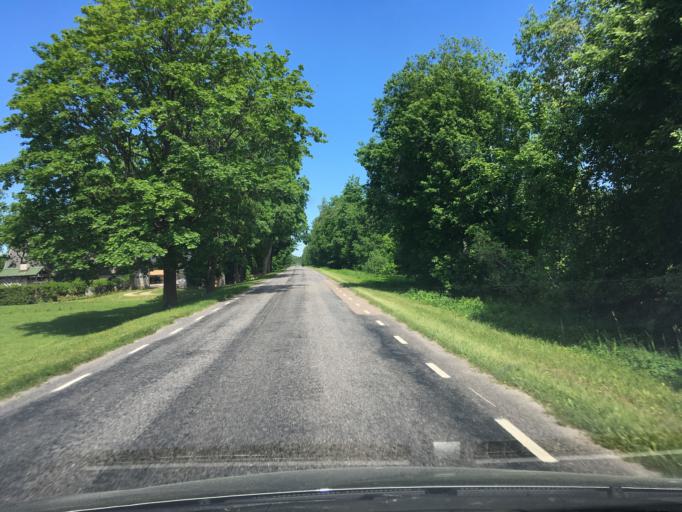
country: EE
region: Raplamaa
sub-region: Rapla vald
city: Rapla
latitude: 59.0602
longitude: 24.9109
